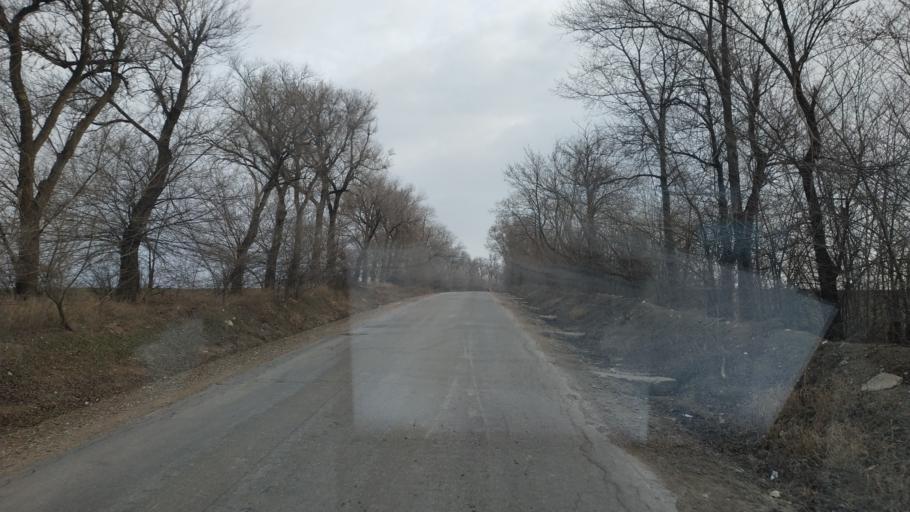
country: MD
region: Chisinau
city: Singera
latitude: 46.9467
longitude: 29.0534
